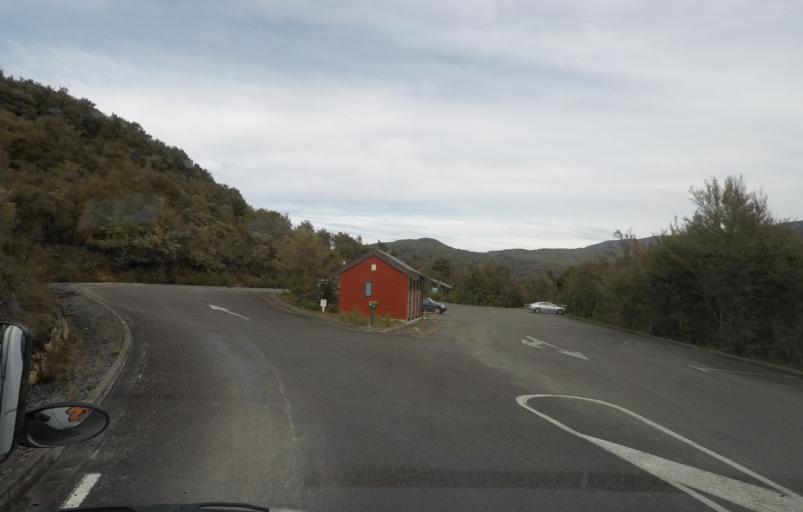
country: NZ
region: Tasman
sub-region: Tasman District
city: Takaka
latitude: -40.8477
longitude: 172.7711
